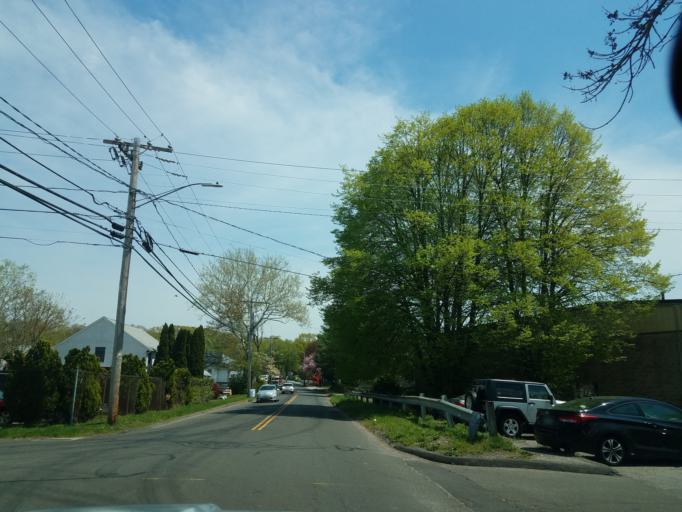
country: US
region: Connecticut
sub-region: Fairfield County
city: Norwalk
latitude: 41.1363
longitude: -73.4281
